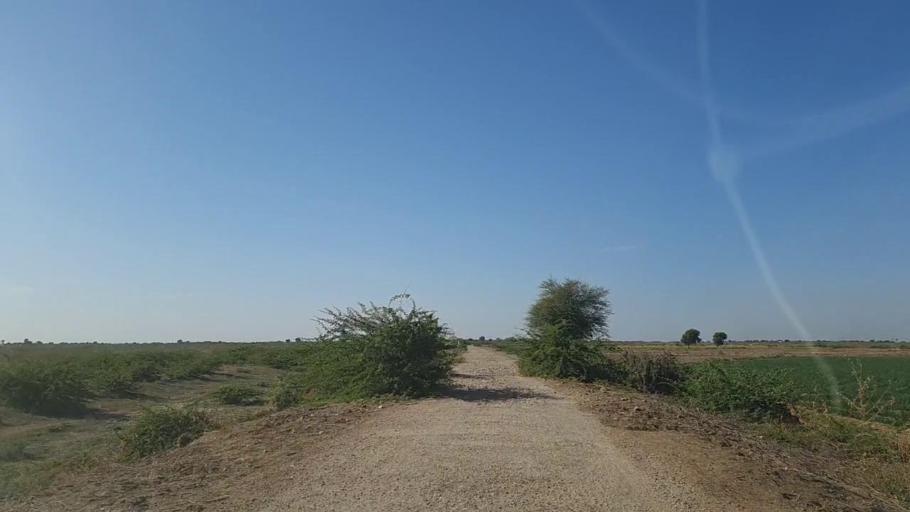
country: PK
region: Sindh
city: Kunri
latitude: 25.2332
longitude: 69.5037
